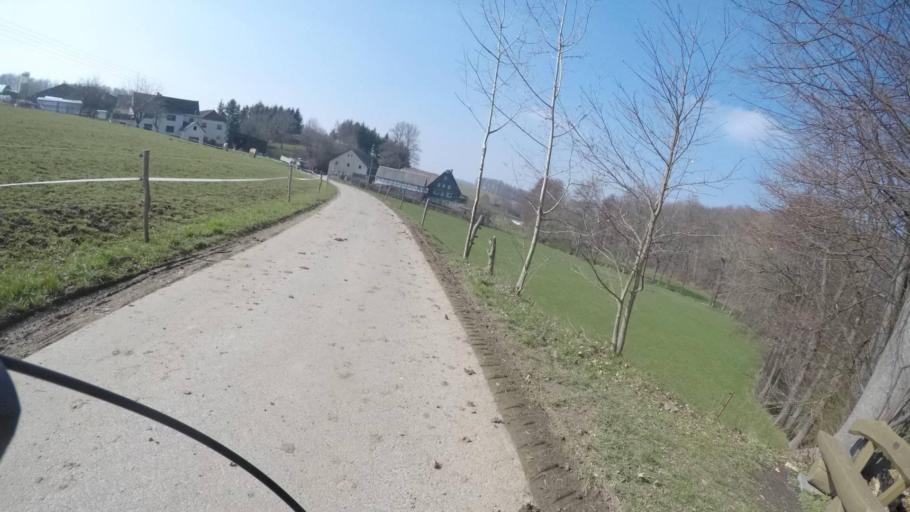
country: DE
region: Saxony
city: Niederfrohna
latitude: 50.8750
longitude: 12.6844
